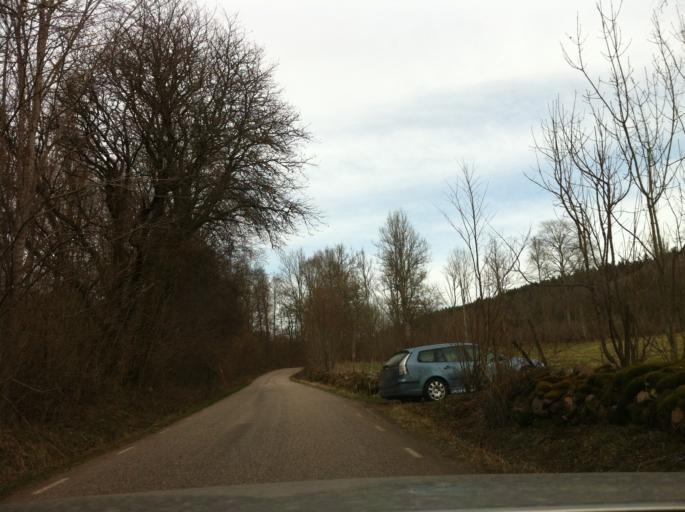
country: SE
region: Vaestra Goetaland
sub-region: Skovde Kommun
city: Skoevde
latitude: 58.4558
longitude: 13.7315
